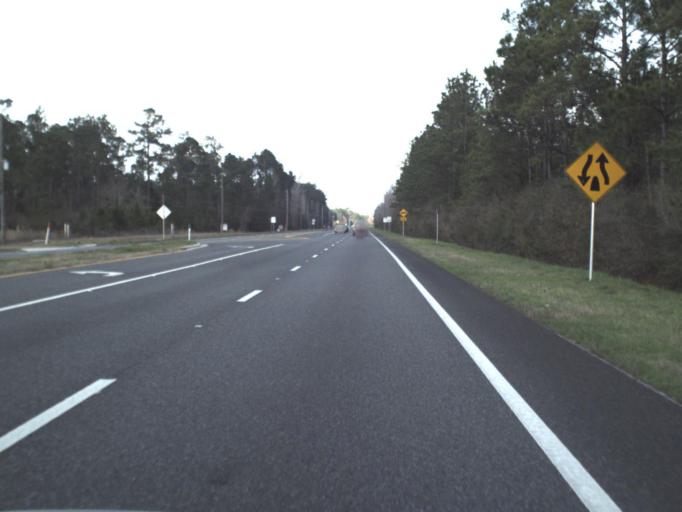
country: US
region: Florida
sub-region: Bay County
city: Youngstown
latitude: 30.4641
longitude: -85.4229
